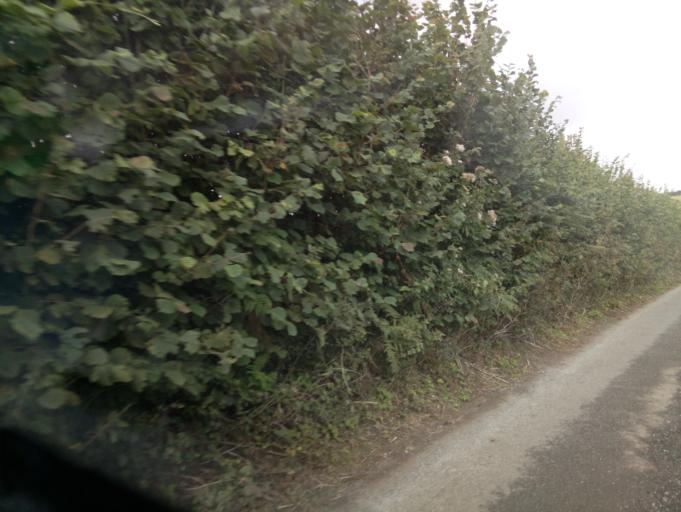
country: GB
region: England
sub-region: Devon
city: Dartmouth
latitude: 50.3341
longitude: -3.5874
